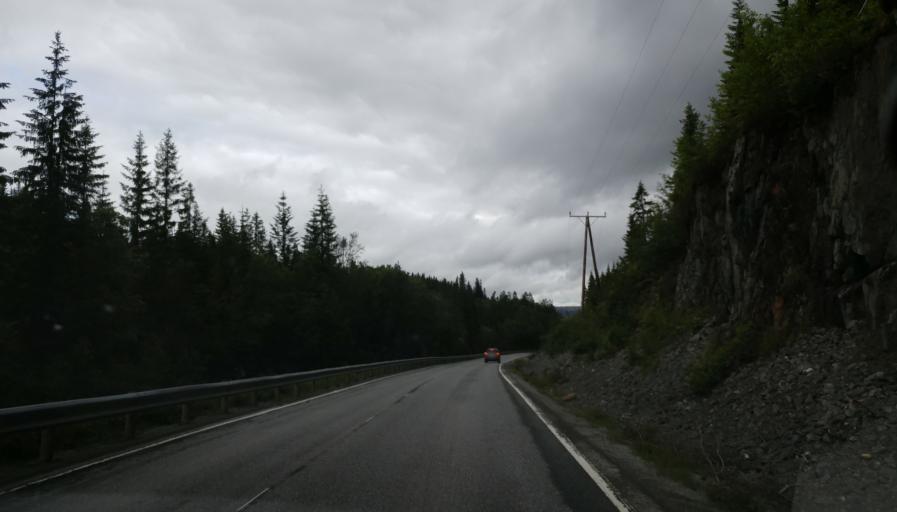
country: NO
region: Sor-Trondelag
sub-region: Selbu
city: Mebonden
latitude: 63.3441
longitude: 11.0769
